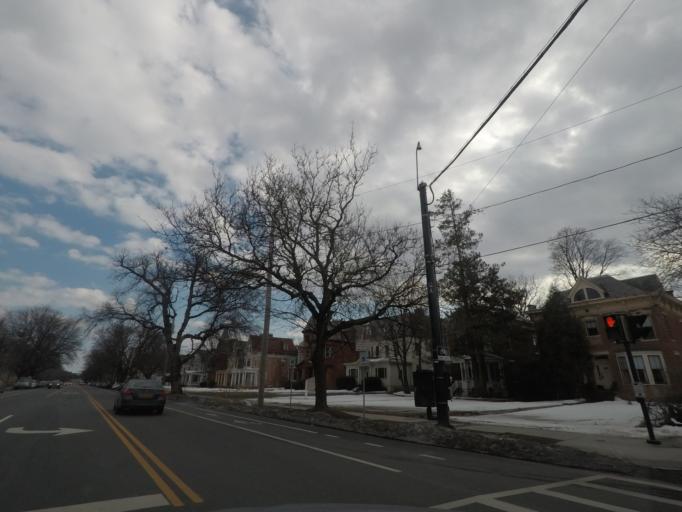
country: US
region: New York
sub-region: Albany County
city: Albany
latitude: 42.6580
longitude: -73.7774
